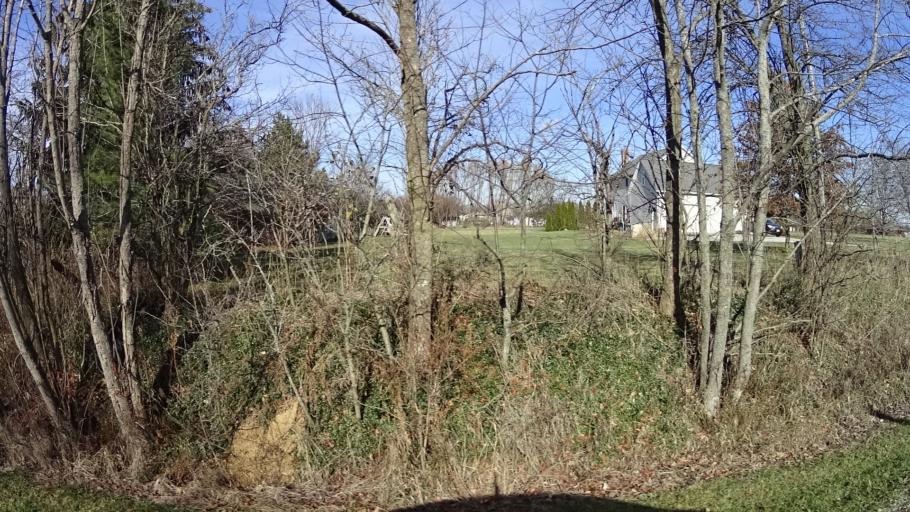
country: US
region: Ohio
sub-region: Lorain County
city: Wellington
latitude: 41.0852
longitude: -82.2412
